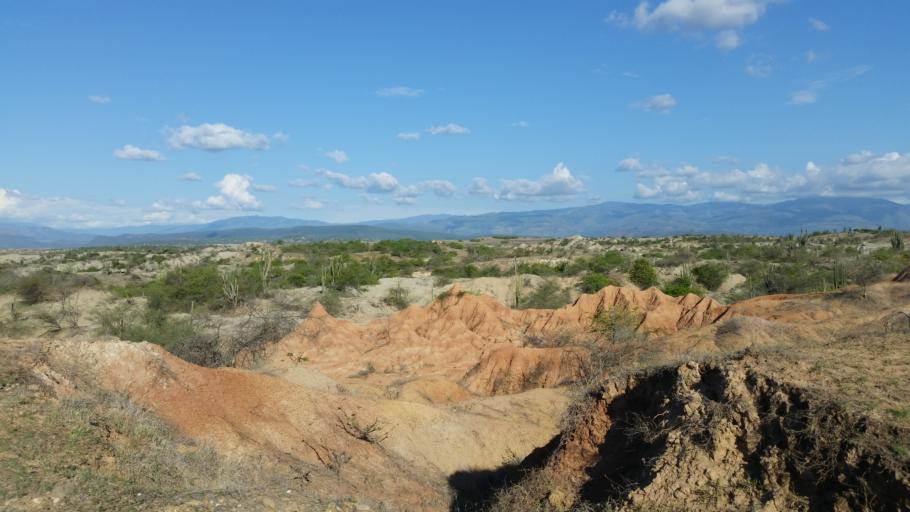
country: CO
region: Huila
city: Villavieja
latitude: 3.2295
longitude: -75.1517
